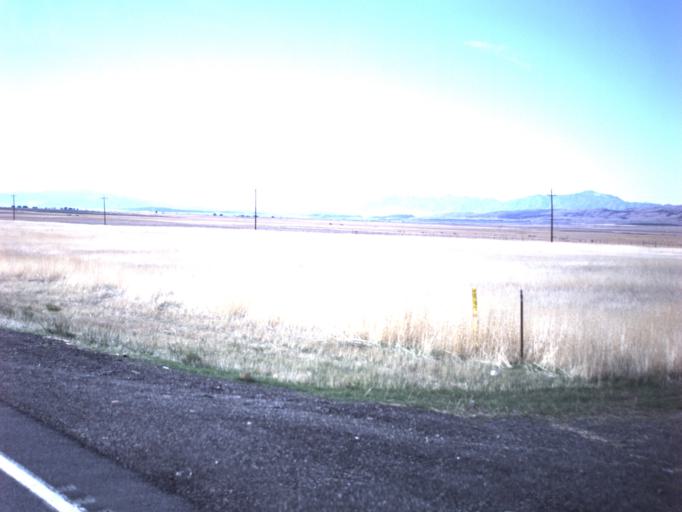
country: US
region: Utah
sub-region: Juab County
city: Nephi
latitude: 39.5948
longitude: -111.8618
